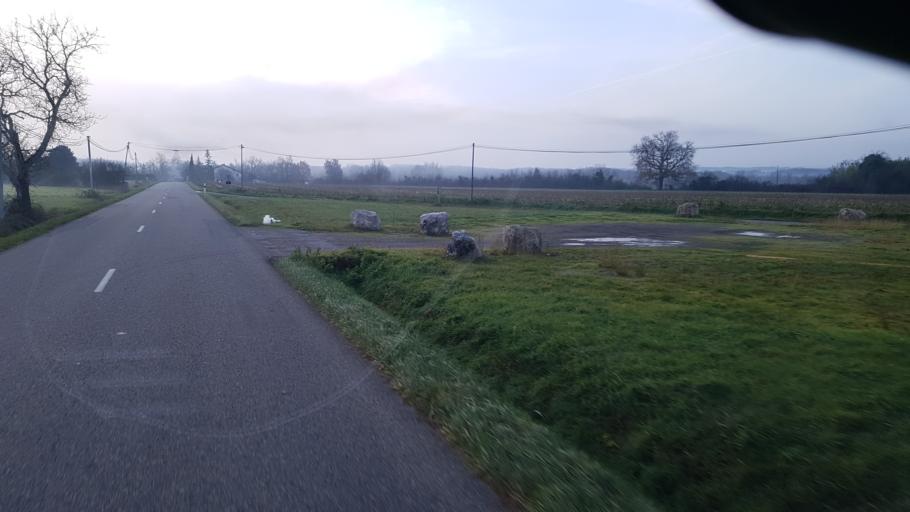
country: FR
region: Midi-Pyrenees
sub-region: Departement du Tarn-et-Garonne
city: Montricoux
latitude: 44.0823
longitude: 1.6136
